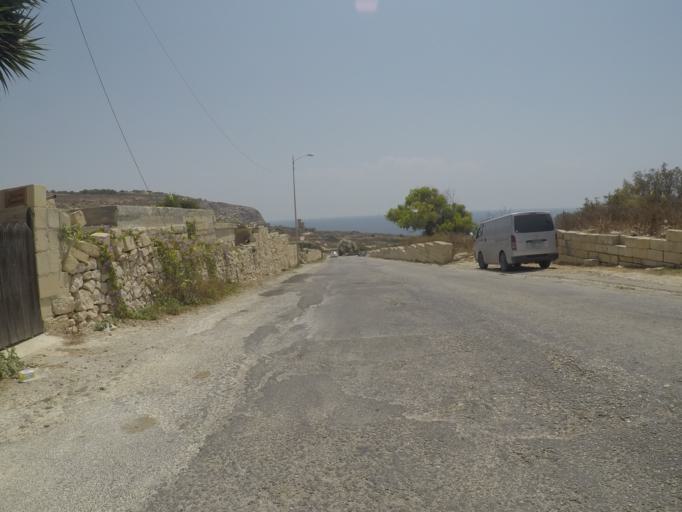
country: MT
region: Is-Siggiewi
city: Siggiewi
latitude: 35.8328
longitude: 14.4182
